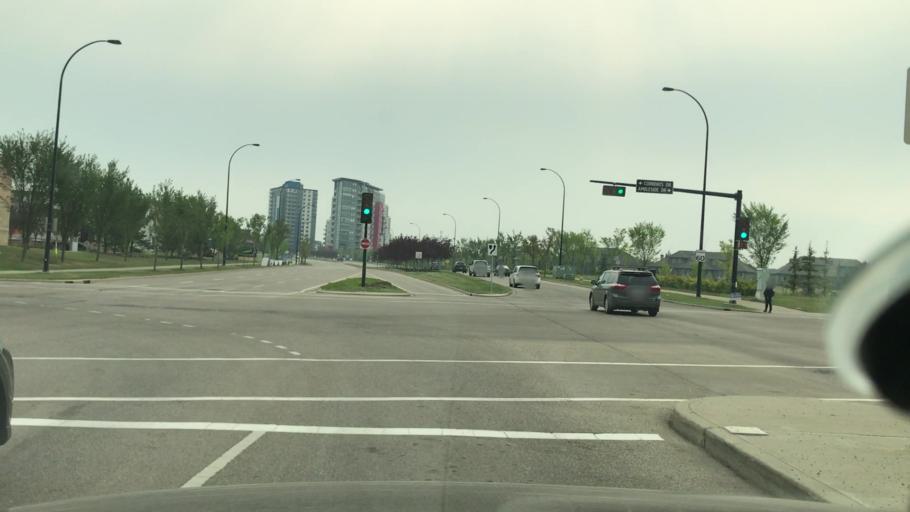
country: CA
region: Alberta
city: Devon
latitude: 53.4353
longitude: -113.6083
